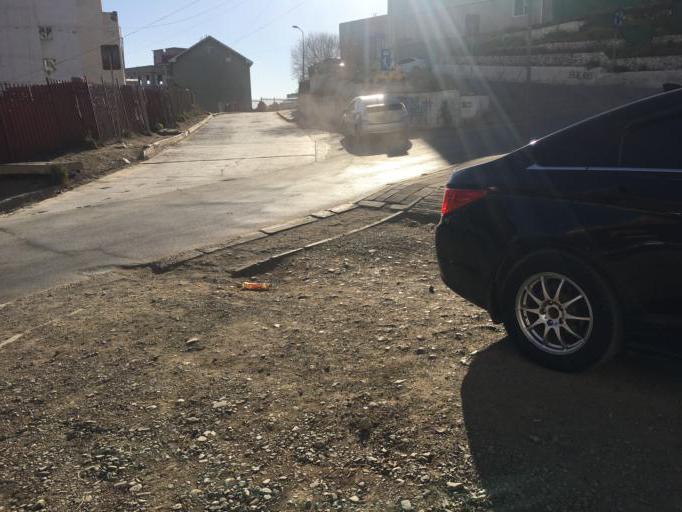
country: MN
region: Ulaanbaatar
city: Ulaanbaatar
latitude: 47.9248
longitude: 106.8666
